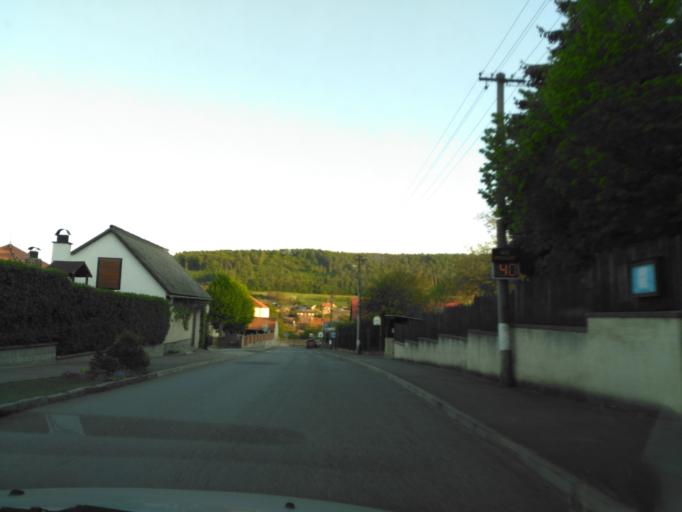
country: CZ
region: Central Bohemia
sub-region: Okres Beroun
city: Kraluv Dvur
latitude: 49.9083
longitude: 14.0332
